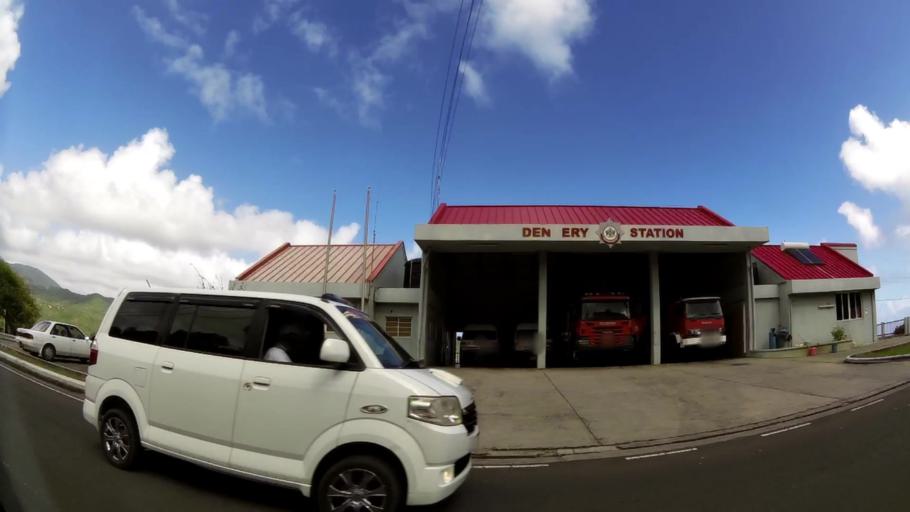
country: LC
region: Dennery Quarter
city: Dennery
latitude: 13.9180
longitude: -60.8929
